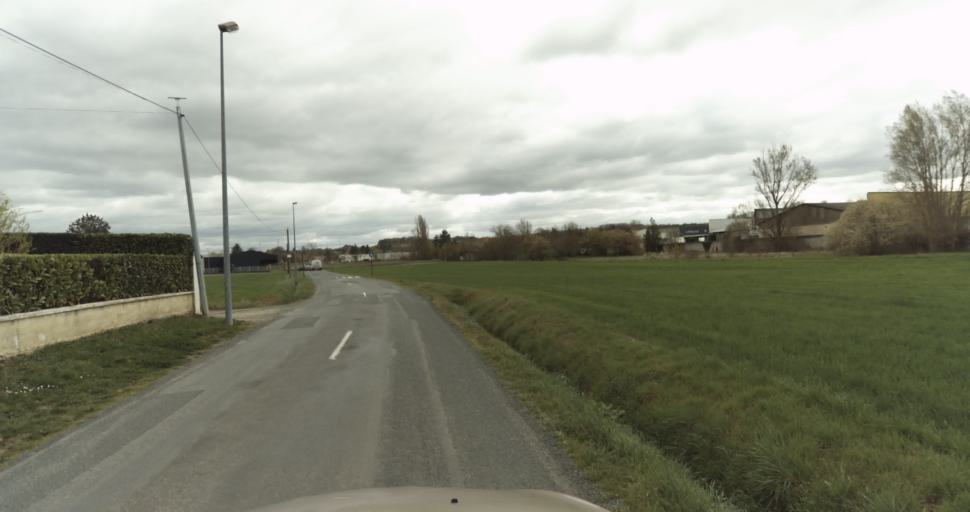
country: FR
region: Midi-Pyrenees
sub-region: Departement du Tarn
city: Puygouzon
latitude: 43.8967
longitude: 2.1549
